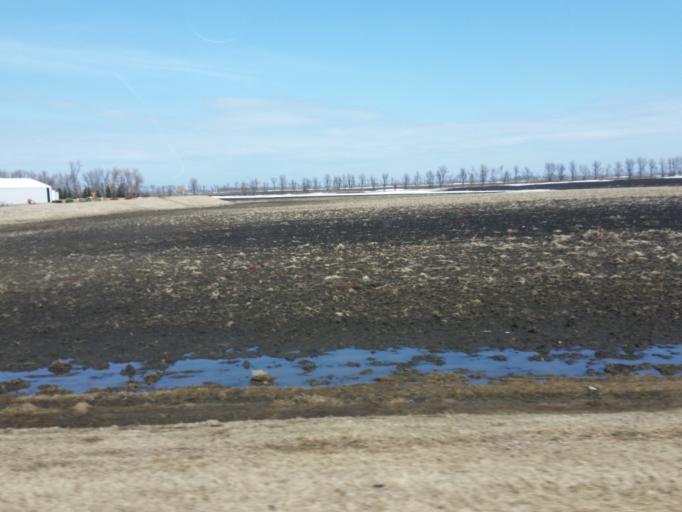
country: US
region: North Dakota
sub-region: Walsh County
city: Grafton
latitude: 48.2955
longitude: -97.2397
